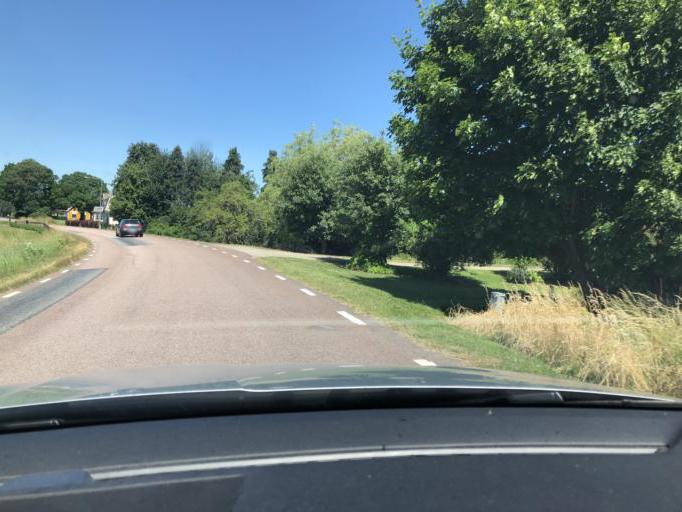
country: SE
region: Blekinge
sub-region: Olofstroms Kommun
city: Jamshog
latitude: 56.1794
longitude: 14.6126
